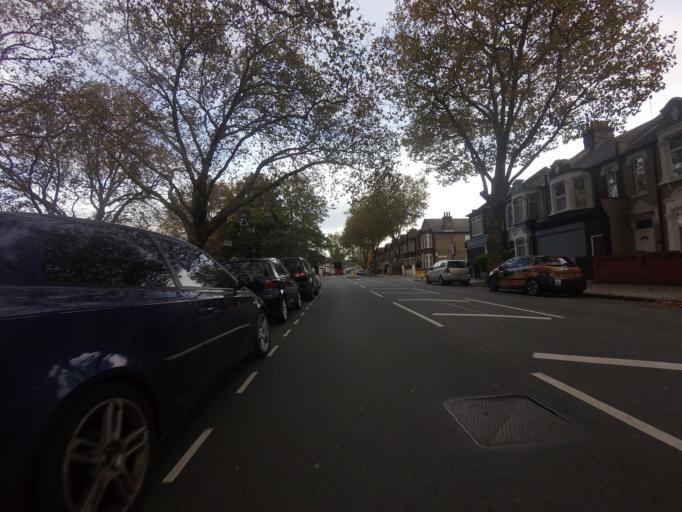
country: GB
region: England
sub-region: Greater London
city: East Ham
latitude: 51.5292
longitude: 0.0560
